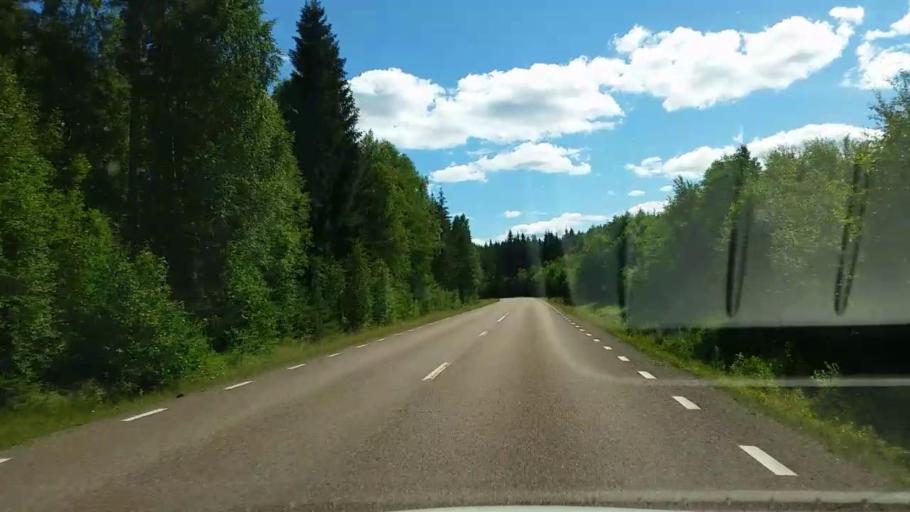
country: SE
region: Dalarna
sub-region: Faluns Kommun
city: Svardsjo
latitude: 60.9604
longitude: 15.6918
